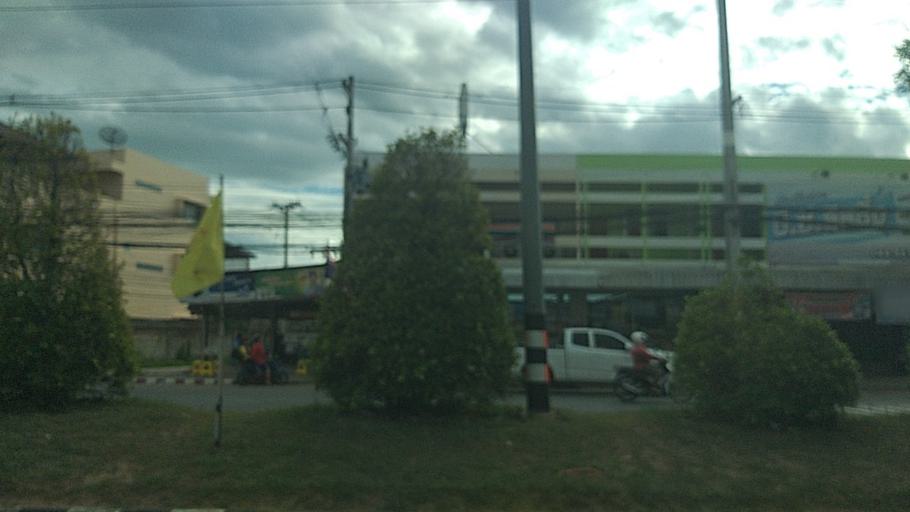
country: TH
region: Surin
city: Prasat
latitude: 14.6350
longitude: 103.4070
